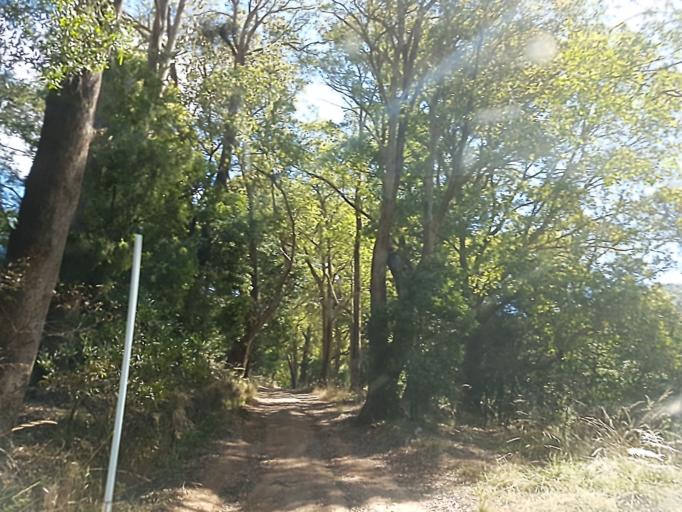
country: AU
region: Victoria
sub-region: Alpine
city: Mount Beauty
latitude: -36.8748
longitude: 147.0556
